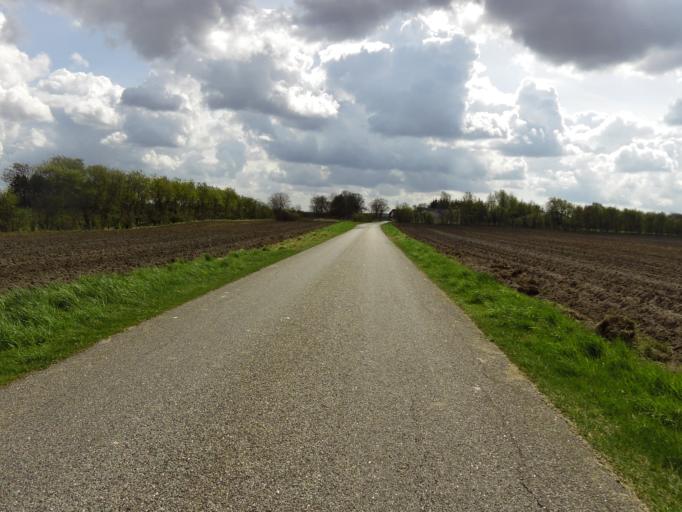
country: DK
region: South Denmark
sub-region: Tonder Kommune
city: Toftlund
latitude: 55.2063
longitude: 9.1638
